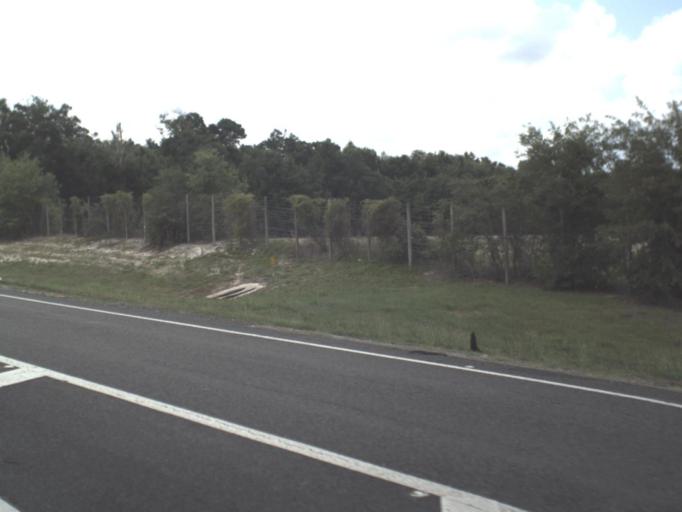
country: US
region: Florida
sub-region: Flagler County
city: Palm Coast
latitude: 29.6651
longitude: -81.2920
